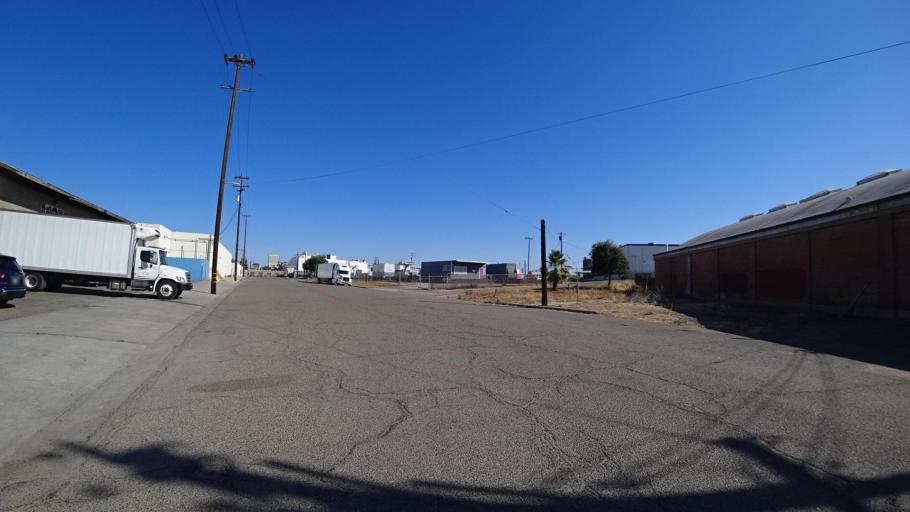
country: US
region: California
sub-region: Fresno County
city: Fresno
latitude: 36.7256
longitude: -119.7774
